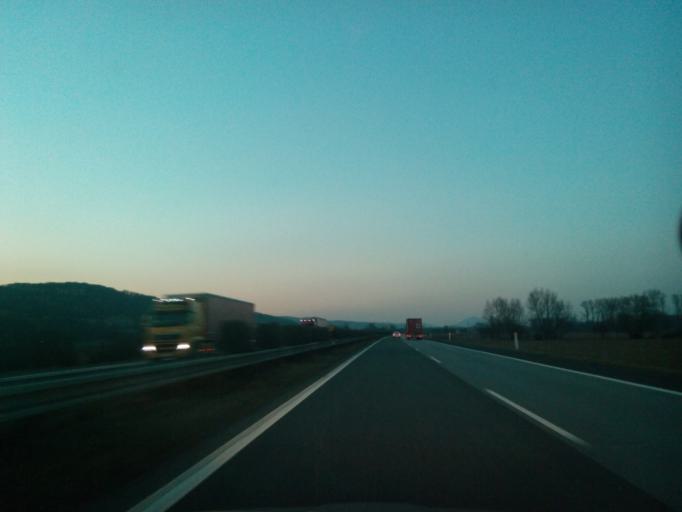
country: SK
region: Presovsky
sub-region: Okres Presov
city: Presov
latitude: 48.8865
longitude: 21.2495
